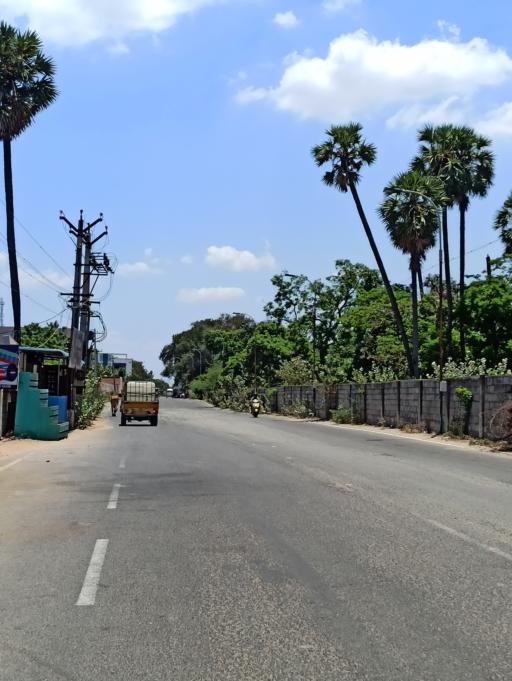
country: IN
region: Tamil Nadu
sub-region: Thiruvallur
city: Chinnasekkadu
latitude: 13.1577
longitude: 80.2358
